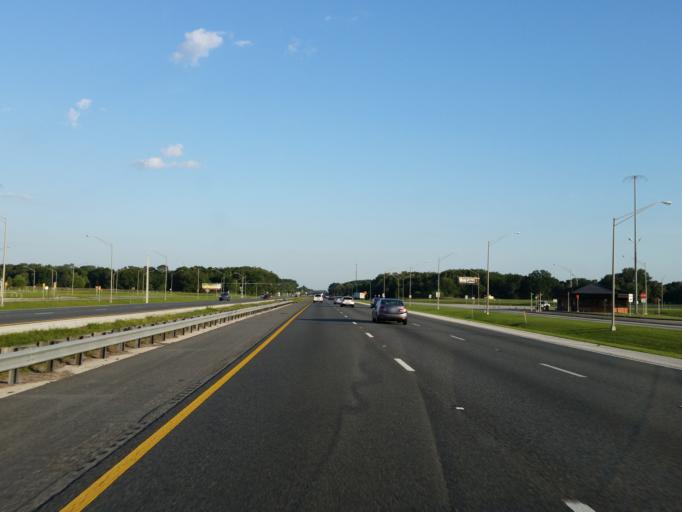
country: US
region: Florida
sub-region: Marion County
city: Belleview
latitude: 28.9944
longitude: -82.1442
